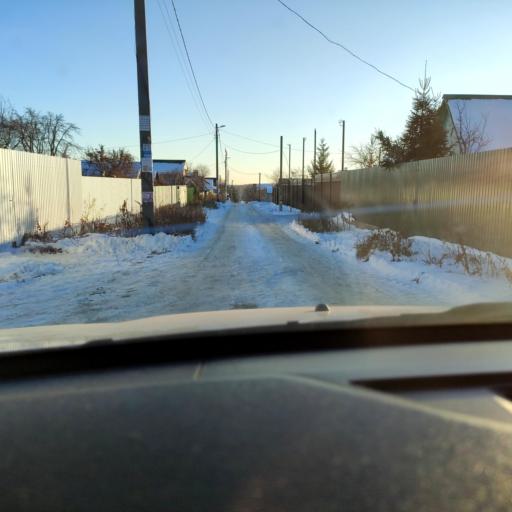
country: RU
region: Samara
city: Petra-Dubrava
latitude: 53.2827
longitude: 50.2921
